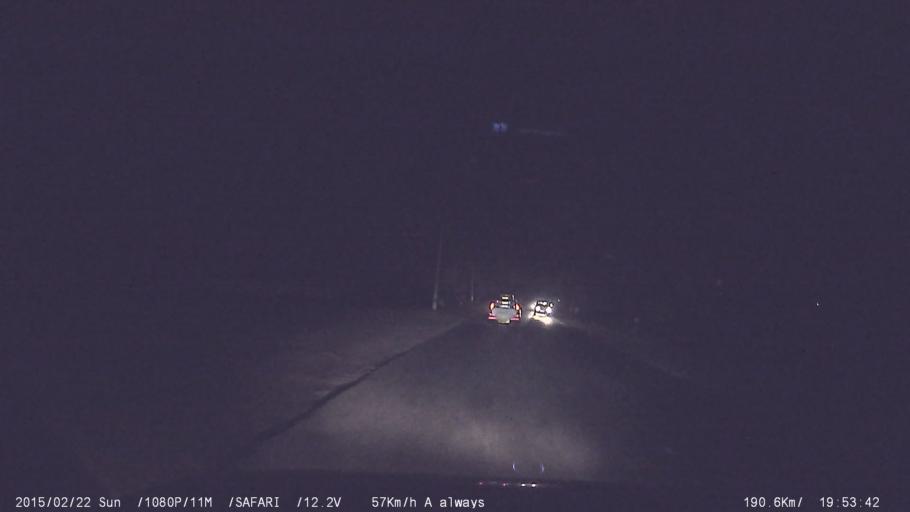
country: IN
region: Tamil Nadu
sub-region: Dindigul
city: Vattalkundu
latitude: 10.1631
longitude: 77.7393
